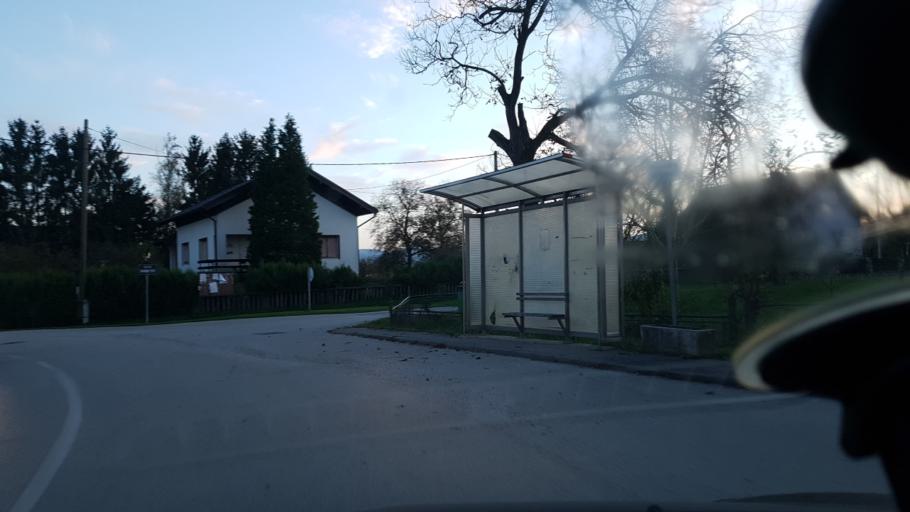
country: HR
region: Zagrebacka
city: Bregana
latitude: 45.8740
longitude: 15.7042
